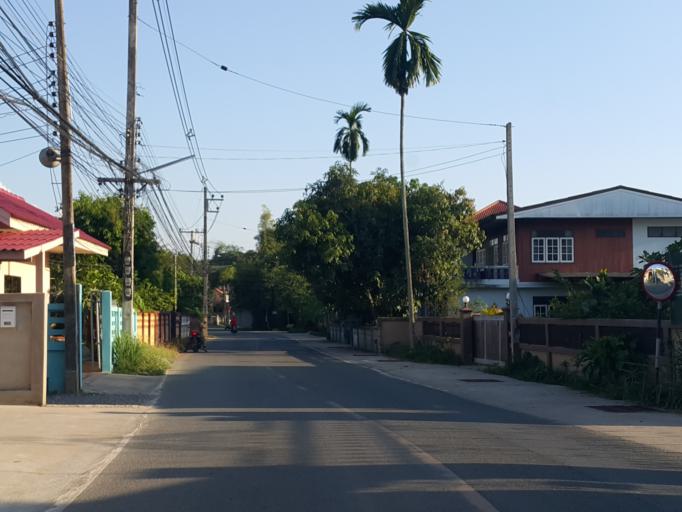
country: TH
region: Chiang Mai
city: San Sai
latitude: 18.7906
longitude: 99.0467
